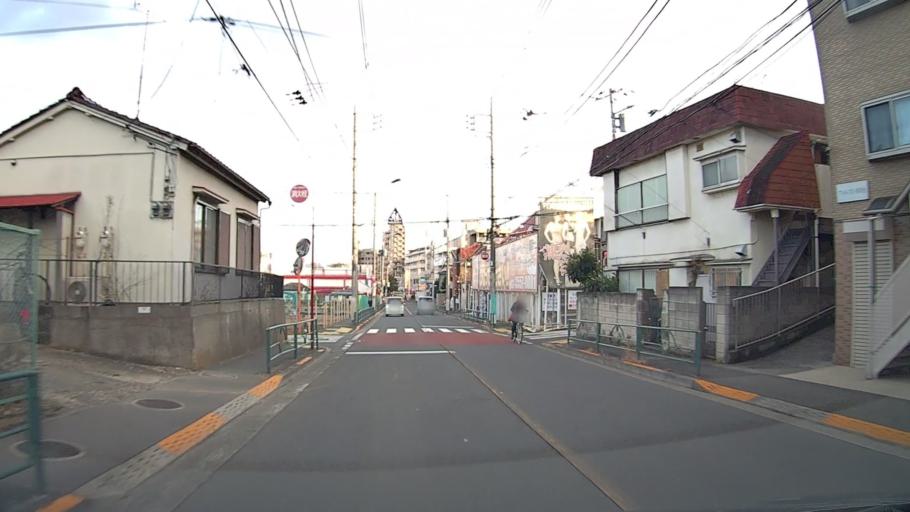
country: JP
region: Saitama
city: Wako
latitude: 35.7516
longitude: 139.6627
